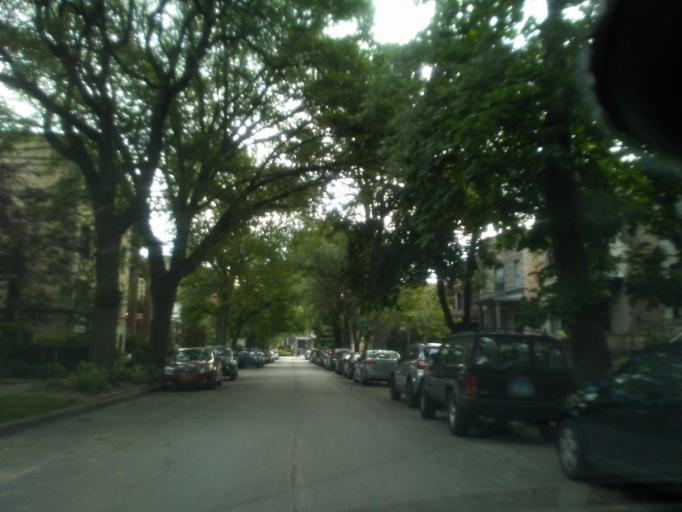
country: US
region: Illinois
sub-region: Cook County
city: Evanston
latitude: 41.9771
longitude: -87.6665
